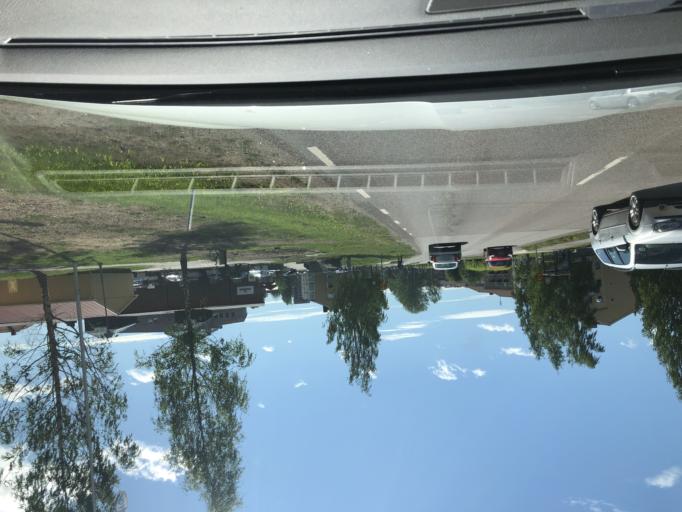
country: SE
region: Norrbotten
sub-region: Pitea Kommun
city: Pitea
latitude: 65.3228
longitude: 21.4636
